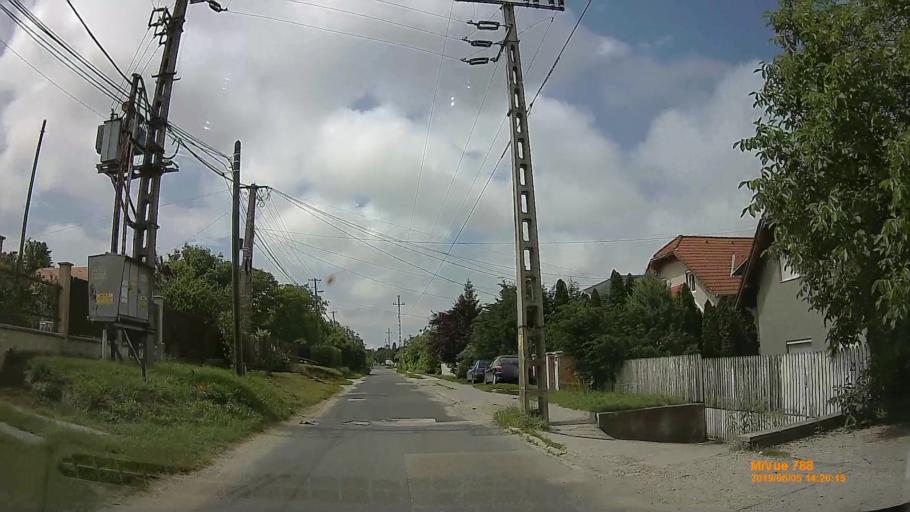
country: HU
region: Pest
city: Kistarcsa
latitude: 47.5577
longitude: 19.2664
